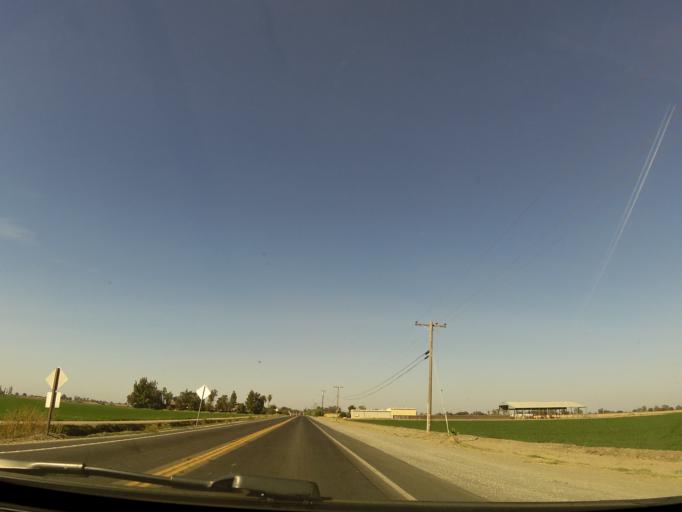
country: US
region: California
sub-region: San Joaquin County
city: Tracy
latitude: 37.8065
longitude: -121.4497
